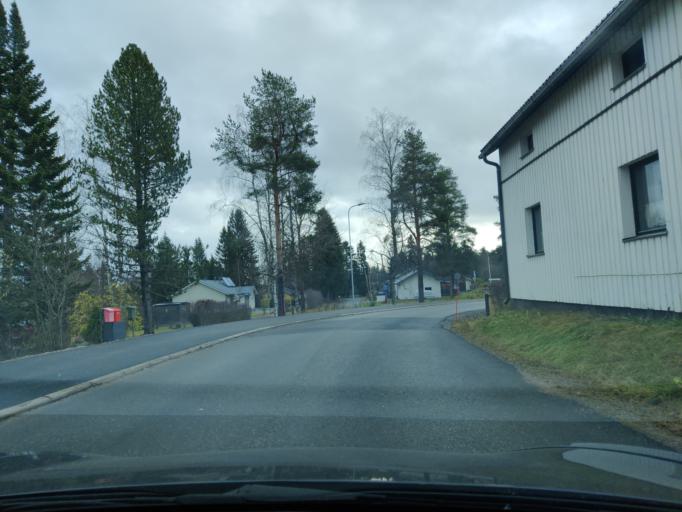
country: FI
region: Northern Savo
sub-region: Ylae-Savo
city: Kiuruvesi
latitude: 63.6494
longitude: 26.6349
